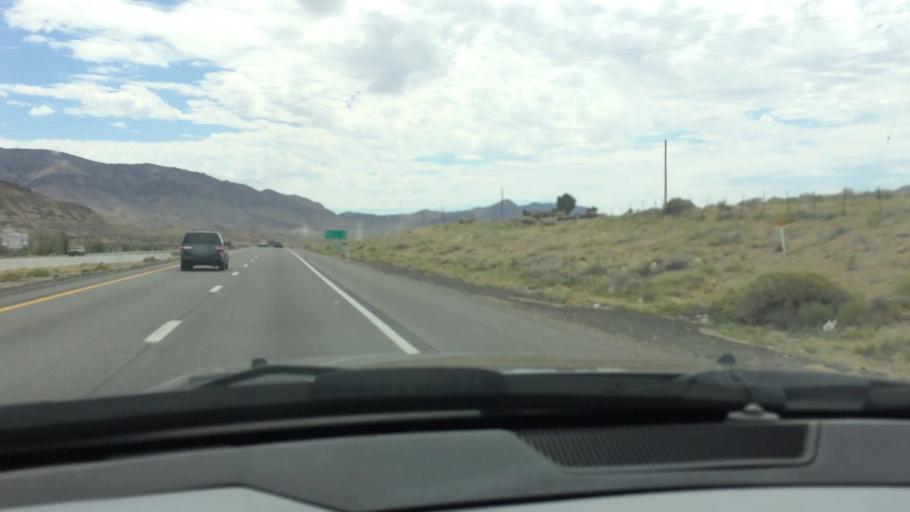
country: US
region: Nevada
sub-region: Lyon County
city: Fernley
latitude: 39.6093
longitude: -119.3210
